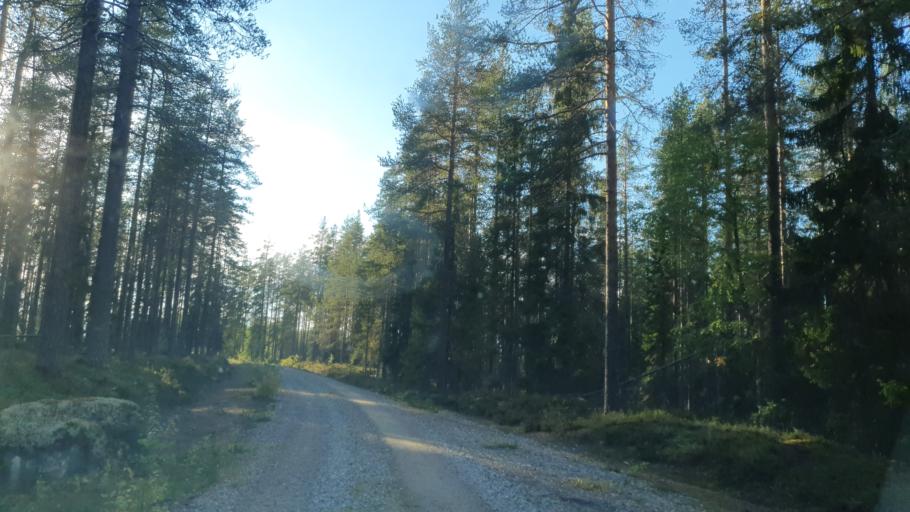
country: FI
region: Kainuu
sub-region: Kehys-Kainuu
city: Kuhmo
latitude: 64.3300
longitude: 30.0233
